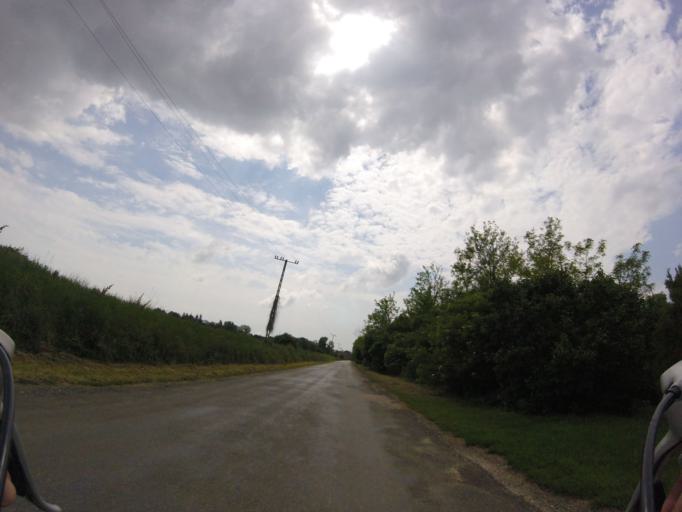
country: HU
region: Baranya
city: Kozarmisleny
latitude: 46.0650
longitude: 18.3716
